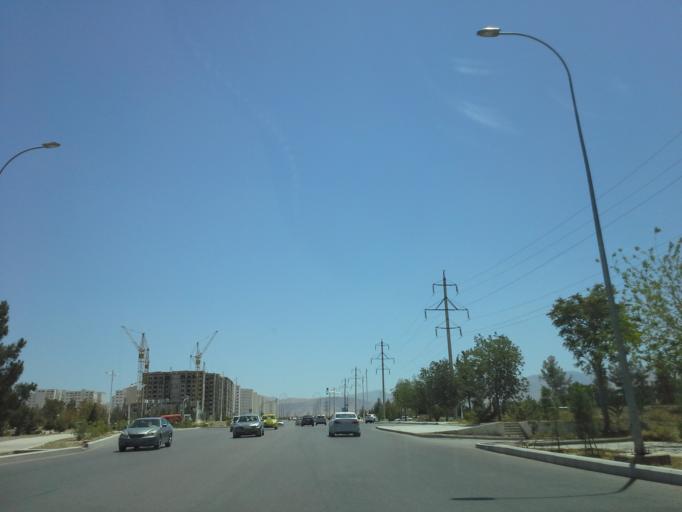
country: TM
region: Ahal
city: Ashgabat
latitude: 37.9020
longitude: 58.4058
